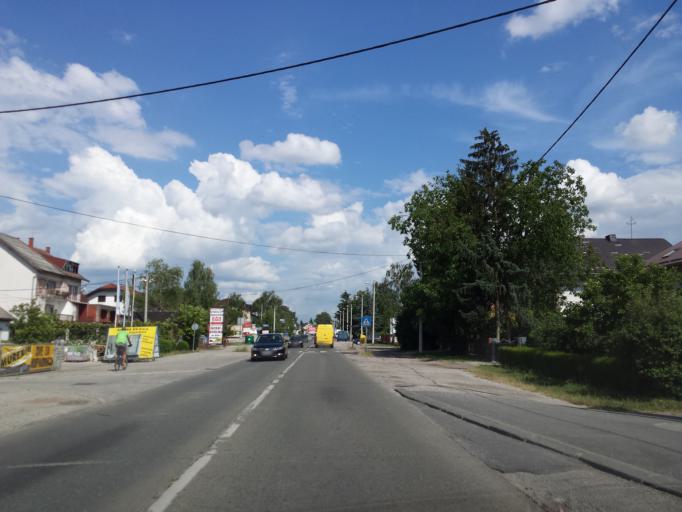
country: HR
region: Grad Zagreb
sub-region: Sesvete
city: Sesvete
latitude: 45.8240
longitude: 16.1529
